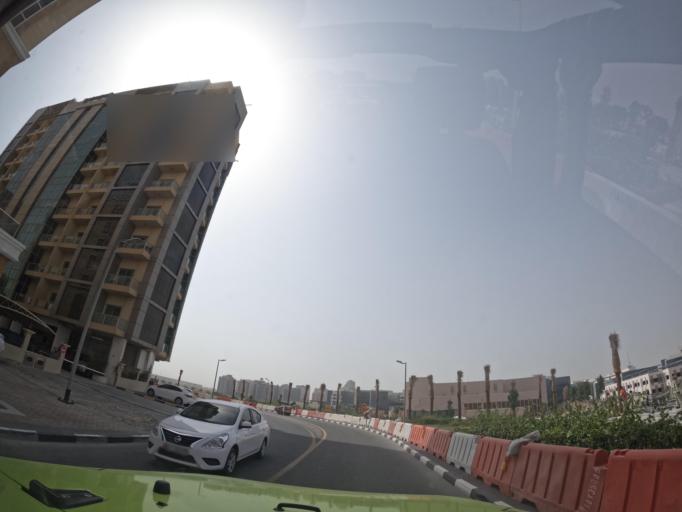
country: AE
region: Dubai
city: Dubai
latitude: 25.1164
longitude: 55.3787
